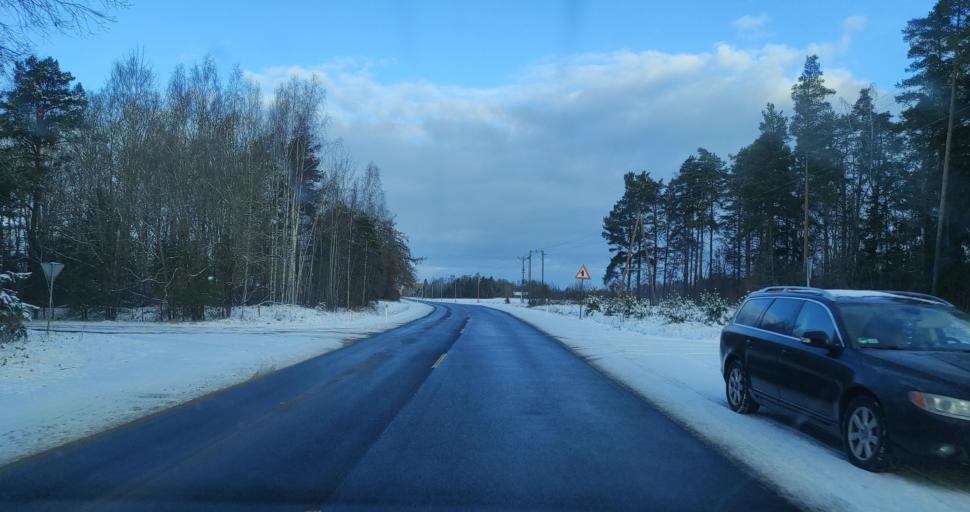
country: LV
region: Skrunda
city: Skrunda
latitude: 56.7335
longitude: 22.0007
